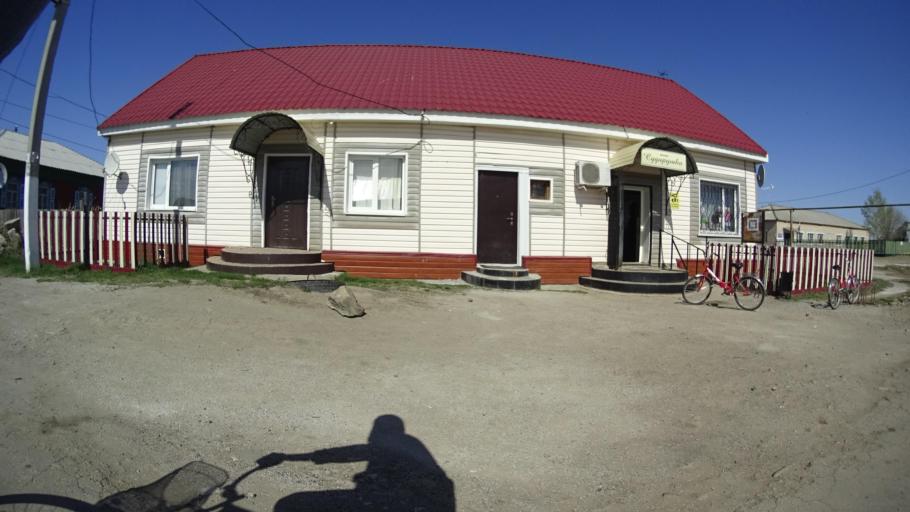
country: RU
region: Chelyabinsk
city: Chesma
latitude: 53.7960
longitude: 61.0327
